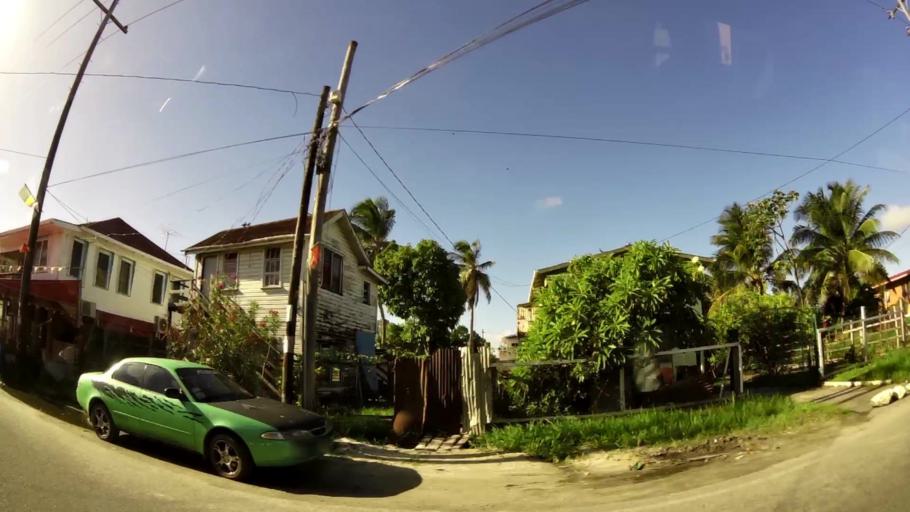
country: GY
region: Demerara-Mahaica
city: Georgetown
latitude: 6.8175
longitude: -58.1422
